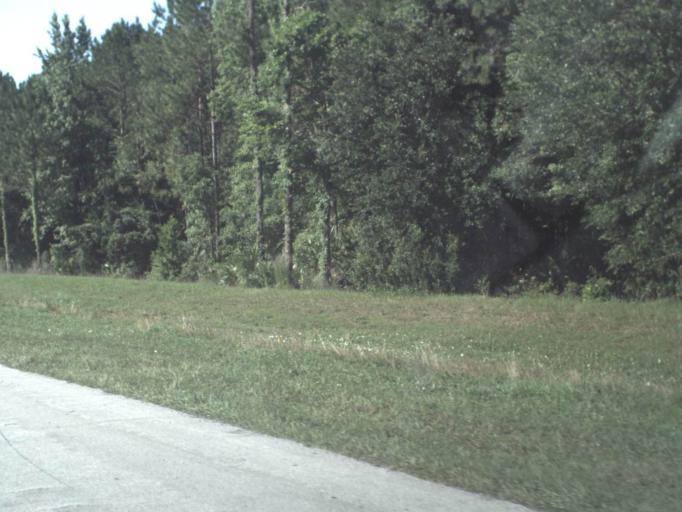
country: US
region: Florida
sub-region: Saint Johns County
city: Villano Beach
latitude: 29.9592
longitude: -81.4457
